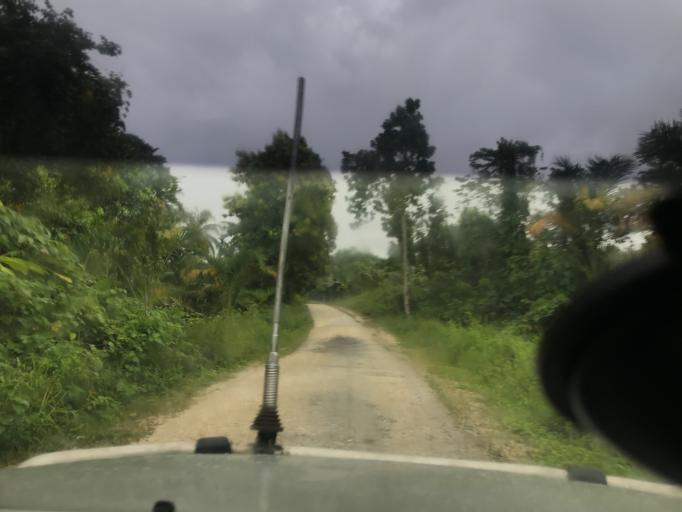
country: SB
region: Malaita
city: Auki
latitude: -9.0021
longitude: 160.7880
